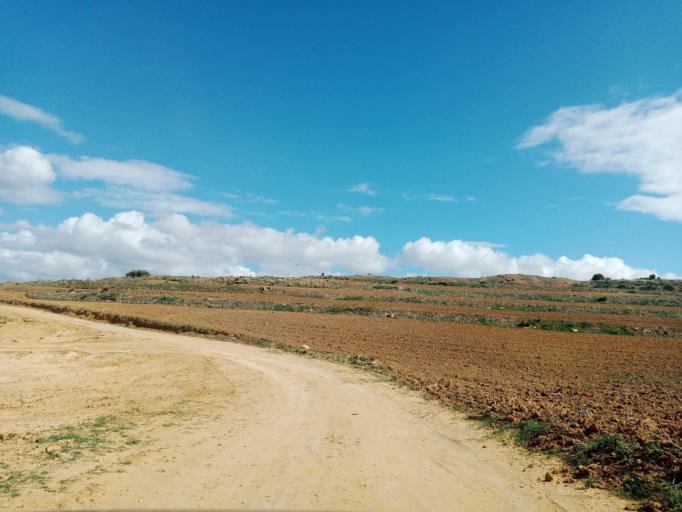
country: TN
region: Tunis
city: Oued Lill
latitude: 36.8147
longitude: 9.9989
